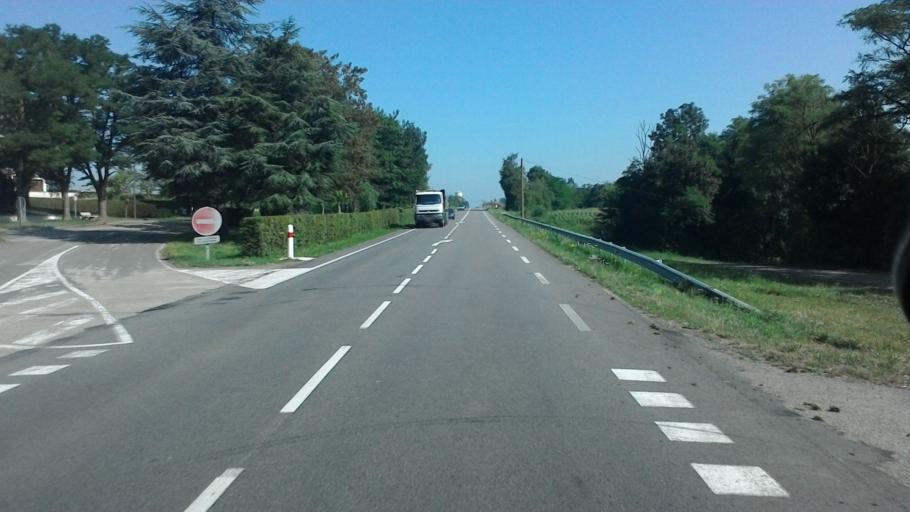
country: FR
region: Rhone-Alpes
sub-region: Departement de l'Ain
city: Montrevel-en-Bresse
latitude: 46.3549
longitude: 5.1241
